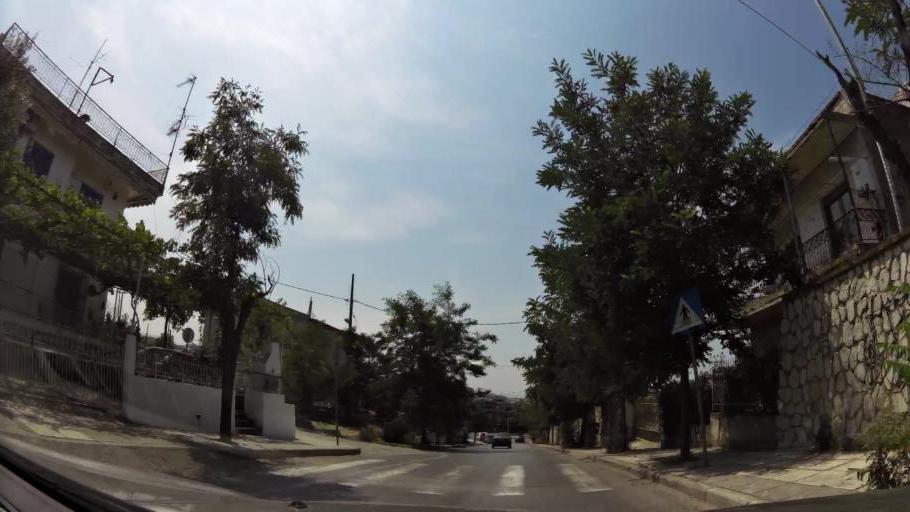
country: GR
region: Central Macedonia
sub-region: Nomos Thessalonikis
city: Triandria
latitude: 40.6270
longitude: 22.9696
